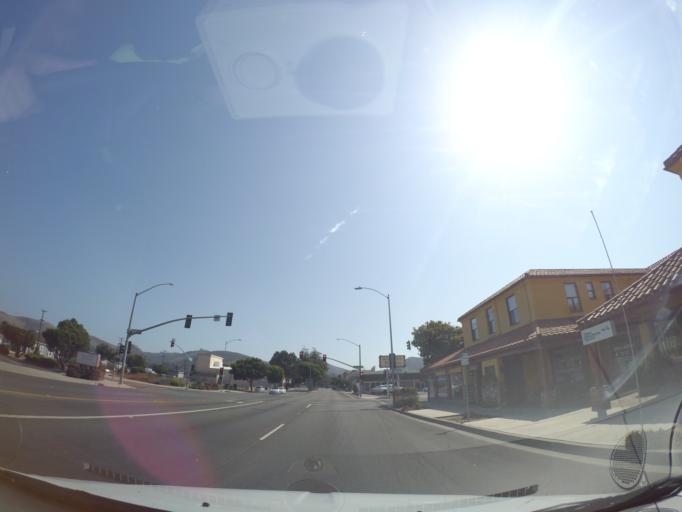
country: US
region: California
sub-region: Santa Barbara County
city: Lompoc
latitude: 34.6410
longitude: -120.4580
